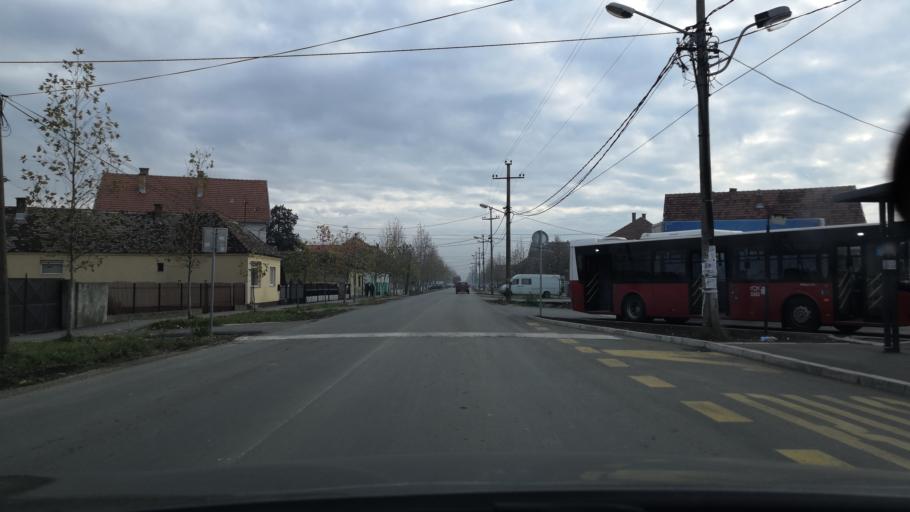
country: RS
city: Ugrinovci
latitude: 44.8782
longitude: 20.1801
